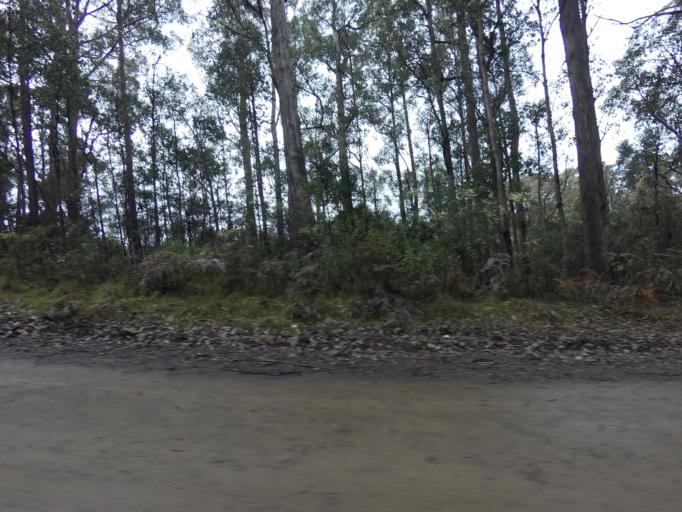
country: AU
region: Tasmania
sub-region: Huon Valley
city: Geeveston
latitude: -43.4483
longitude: 146.9053
